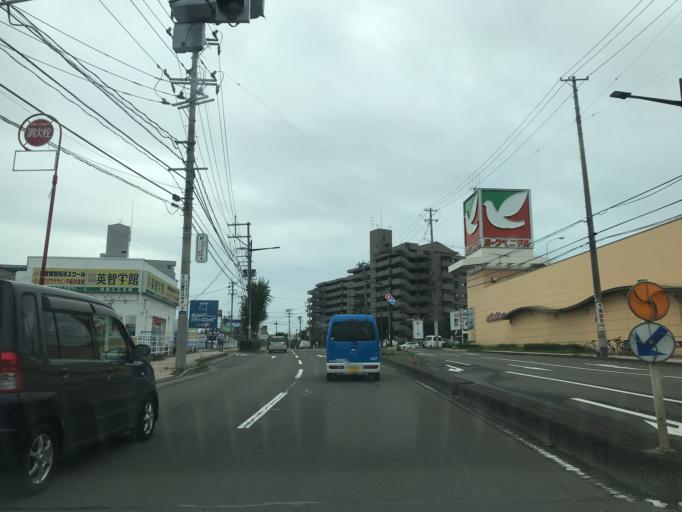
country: JP
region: Miyagi
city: Sendai-shi
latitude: 38.3114
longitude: 140.8879
